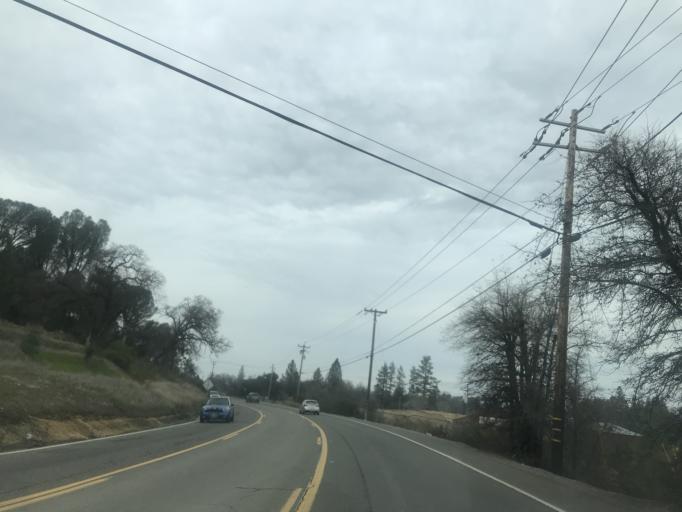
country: US
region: California
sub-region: El Dorado County
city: Diamond Springs
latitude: 38.7012
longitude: -120.8230
